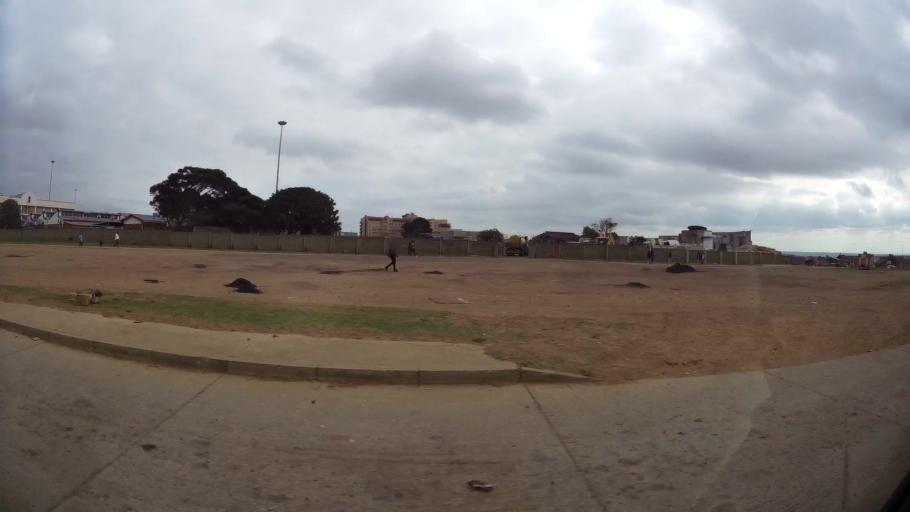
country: ZA
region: Eastern Cape
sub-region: Nelson Mandela Bay Metropolitan Municipality
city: Port Elizabeth
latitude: -33.8813
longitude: 25.5638
